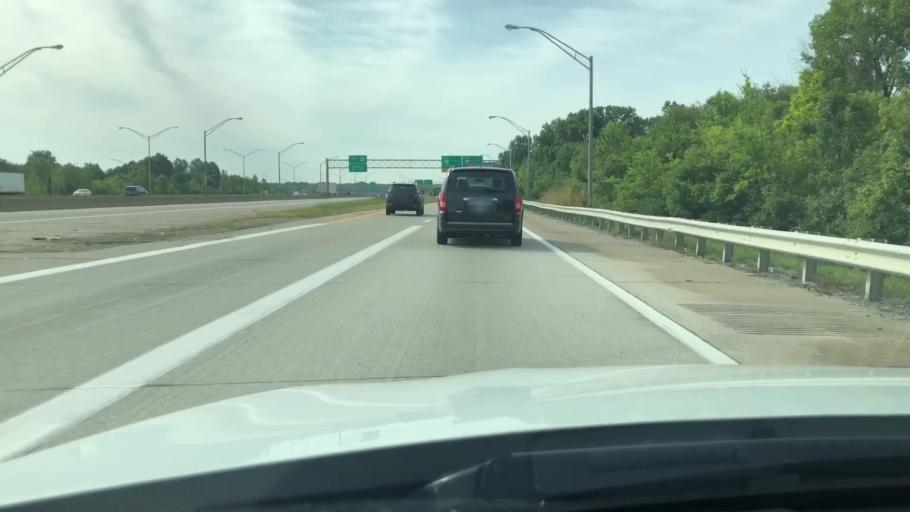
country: US
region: Kentucky
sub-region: Jefferson County
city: Heritage Creek
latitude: 38.1447
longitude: -85.7115
